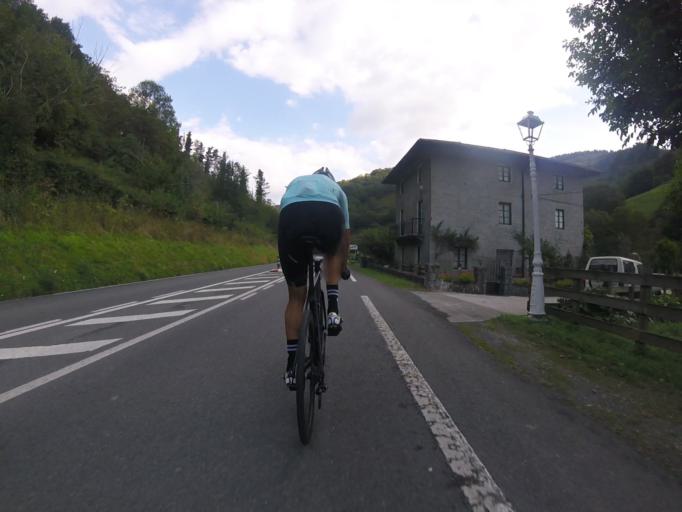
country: ES
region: Basque Country
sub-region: Provincia de Guipuzcoa
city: Amezqueta
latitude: 43.0685
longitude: -2.0845
